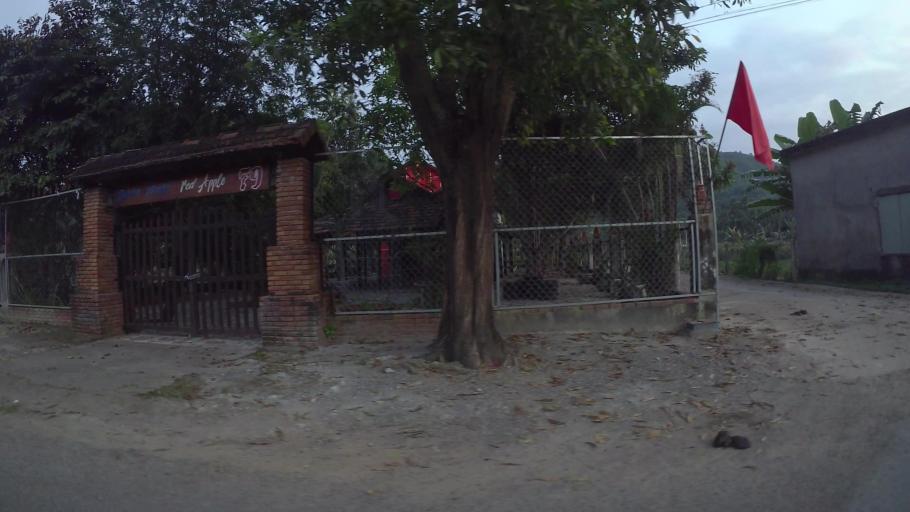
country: VN
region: Da Nang
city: Lien Chieu
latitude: 16.0574
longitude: 108.1187
